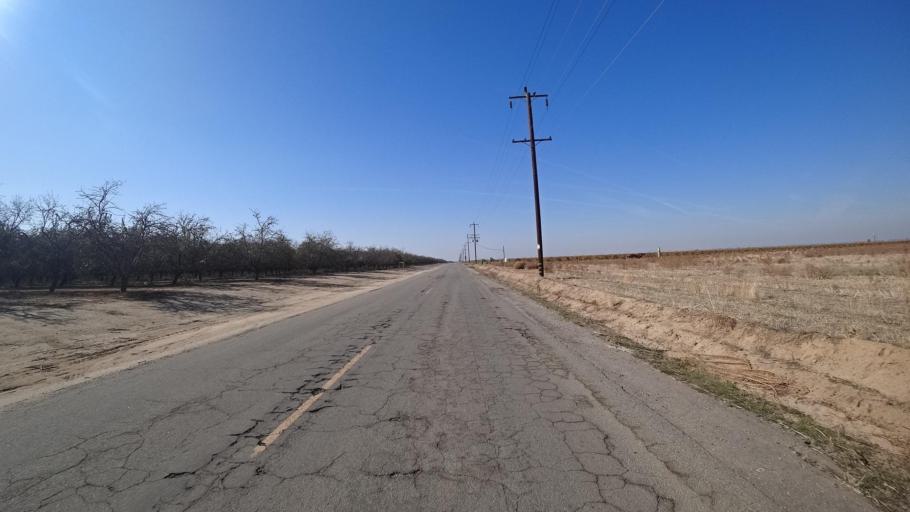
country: US
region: California
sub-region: Kern County
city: McFarland
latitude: 35.7034
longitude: -119.1591
